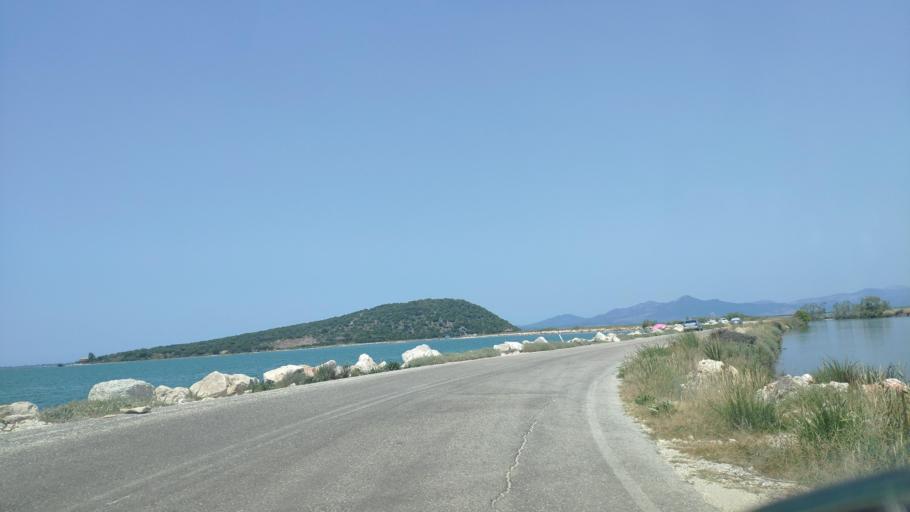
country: GR
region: Epirus
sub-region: Nomos Artas
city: Aneza
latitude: 39.0334
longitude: 20.8852
